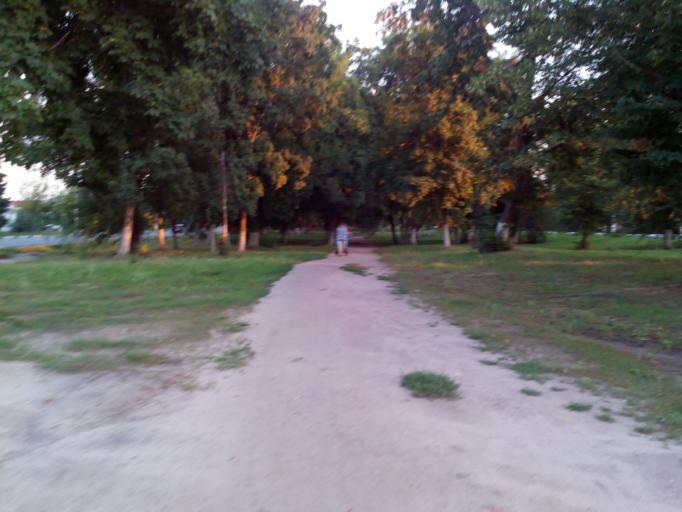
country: RU
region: Voronezj
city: Borisoglebsk
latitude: 51.3593
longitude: 42.0761
